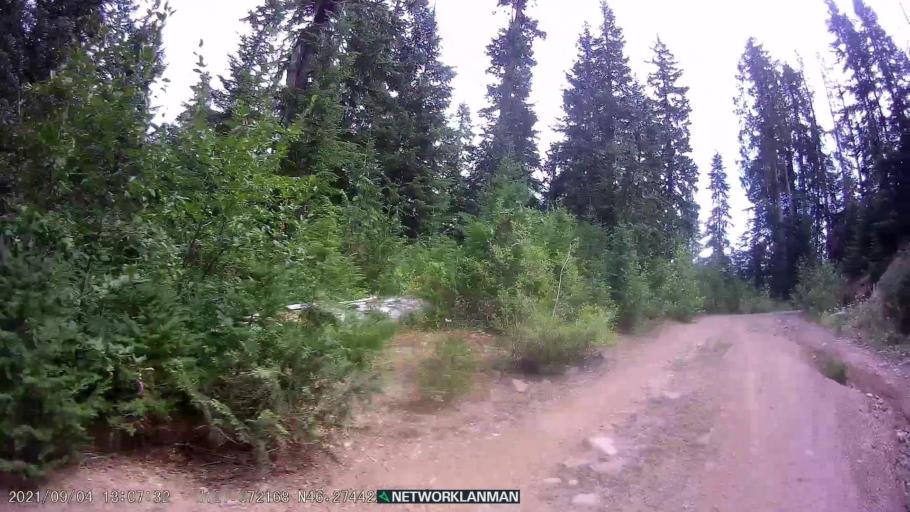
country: US
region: Washington
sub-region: Skamania County
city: Carson
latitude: 46.2744
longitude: -121.6724
